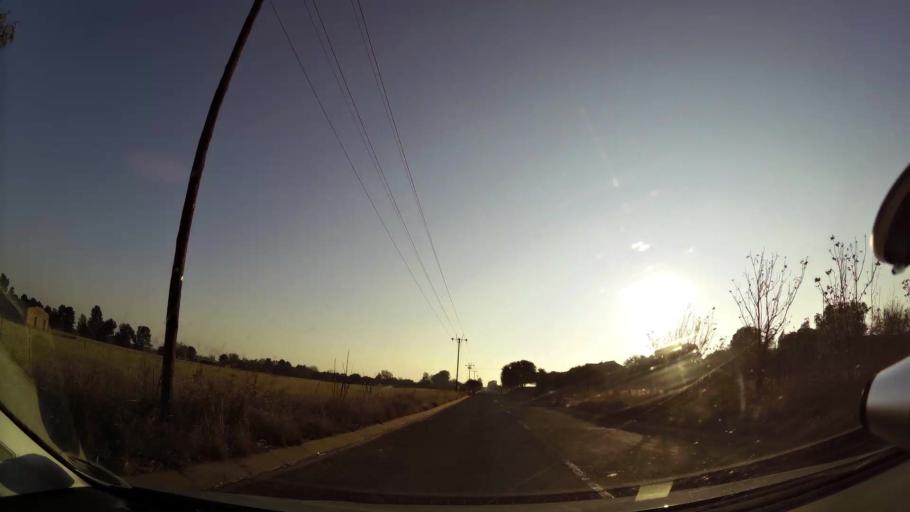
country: ZA
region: Orange Free State
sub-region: Mangaung Metropolitan Municipality
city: Bloemfontein
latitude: -29.0874
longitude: 26.1428
